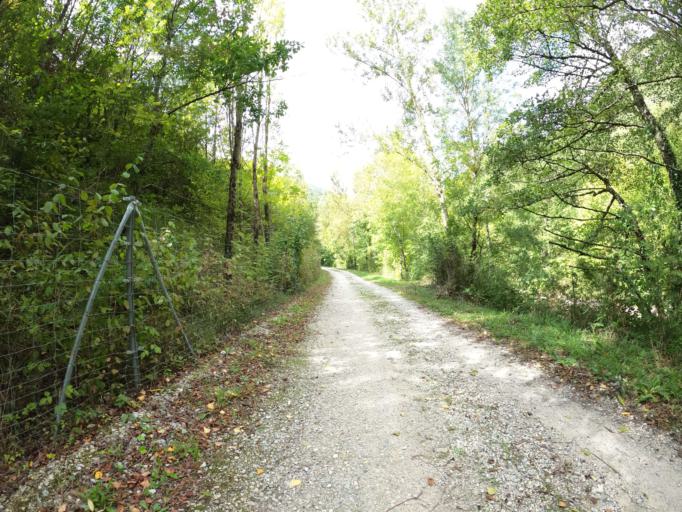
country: ES
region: Navarre
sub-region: Provincia de Navarra
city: Irurtzun
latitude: 42.9425
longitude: -1.8242
